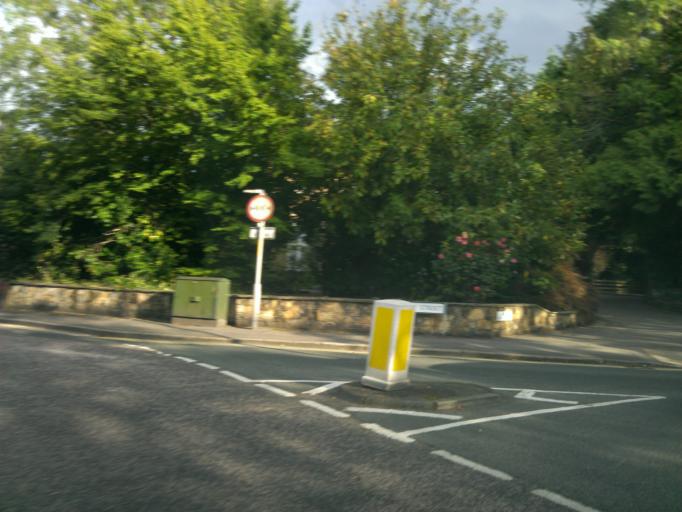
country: GB
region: England
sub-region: Kent
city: Tonbridge
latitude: 51.1977
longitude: 0.2792
